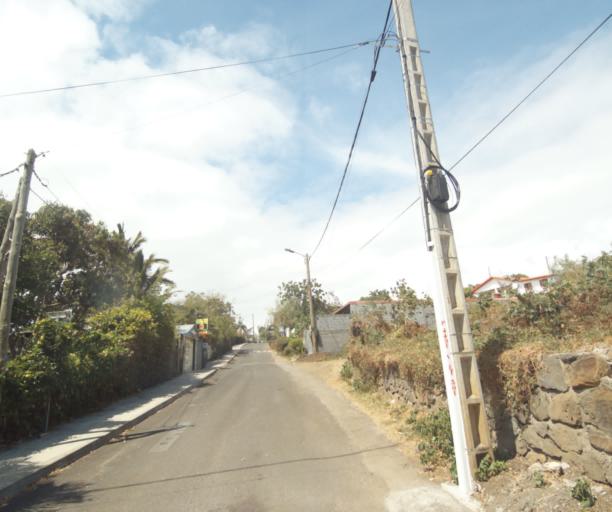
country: RE
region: Reunion
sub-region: Reunion
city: Saint-Paul
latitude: -21.0553
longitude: 55.2566
